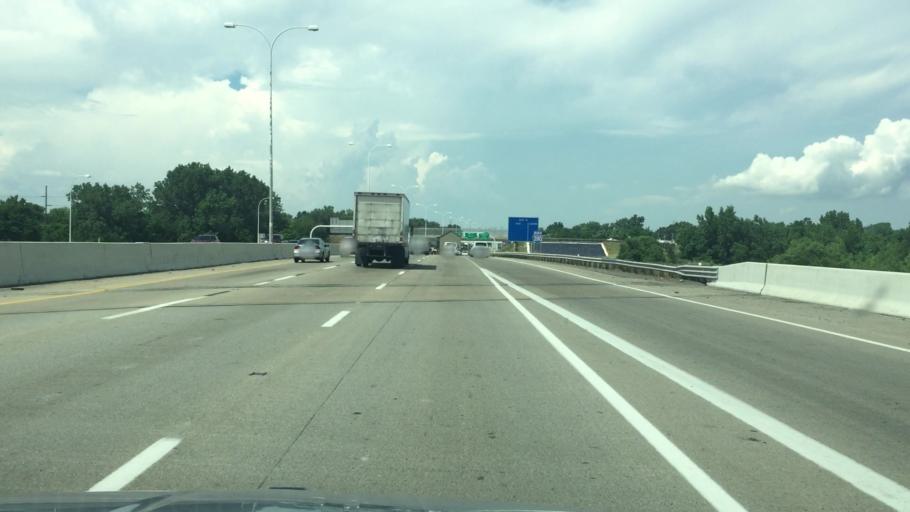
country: US
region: Ohio
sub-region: Lucas County
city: Toledo
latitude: 41.6755
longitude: -83.5152
